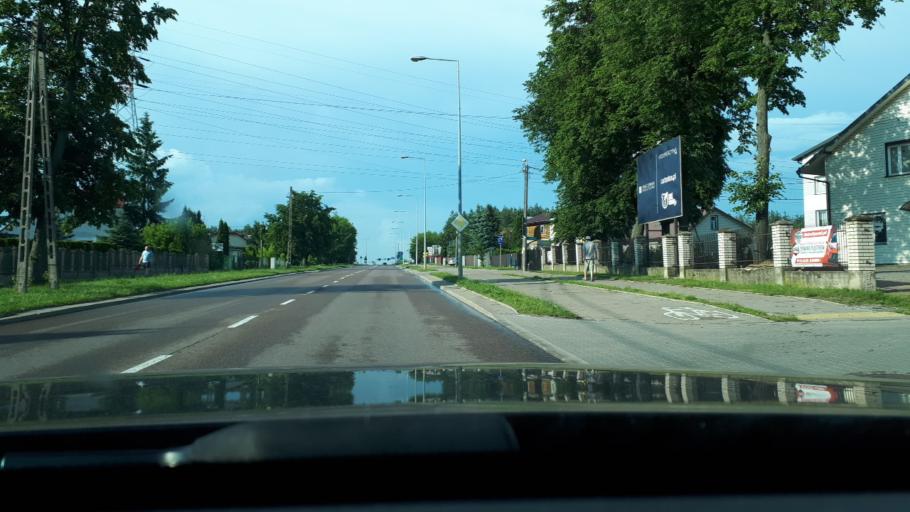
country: PL
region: Podlasie
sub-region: Bialystok
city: Bialystok
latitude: 53.1571
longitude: 23.1960
